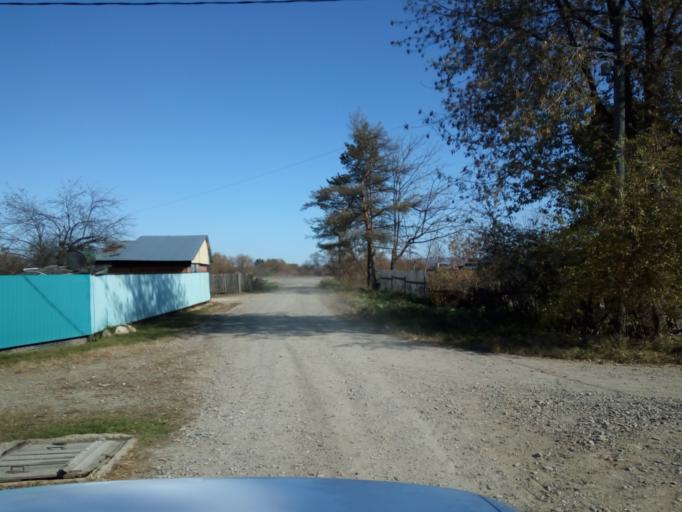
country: RU
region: Primorskiy
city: Dal'nerechensk
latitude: 45.9124
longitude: 133.7915
